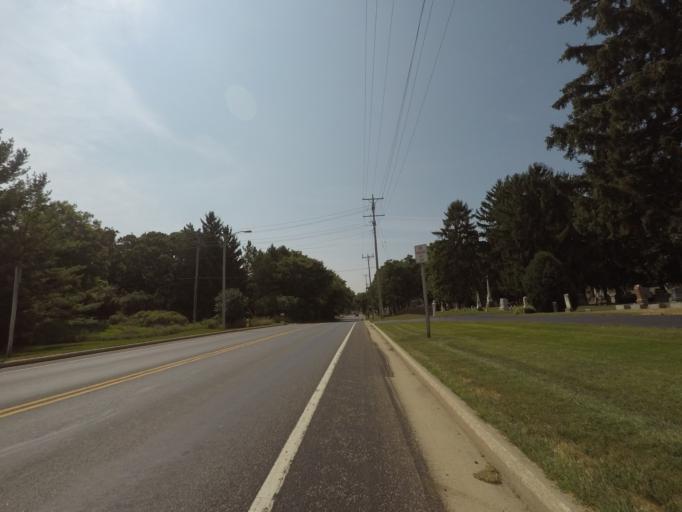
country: US
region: Wisconsin
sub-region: Jefferson County
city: Fort Atkinson
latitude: 42.9417
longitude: -88.8385
